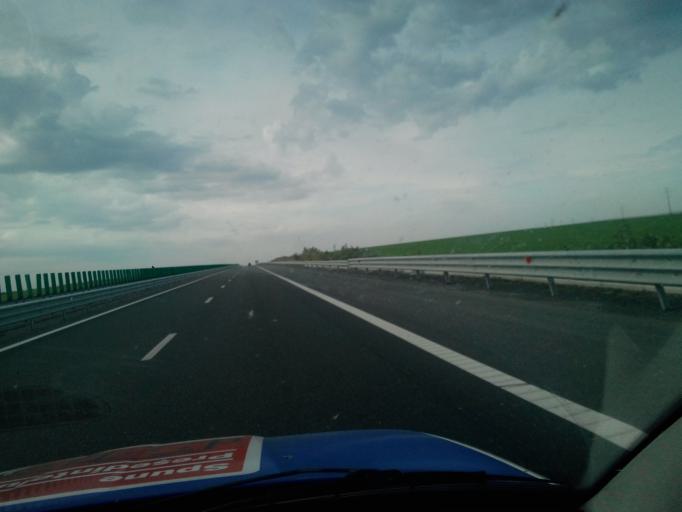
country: RO
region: Constanta
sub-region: Comuna Valu lui Traian
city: Valu lui Traian
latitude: 44.1415
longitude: 28.4848
